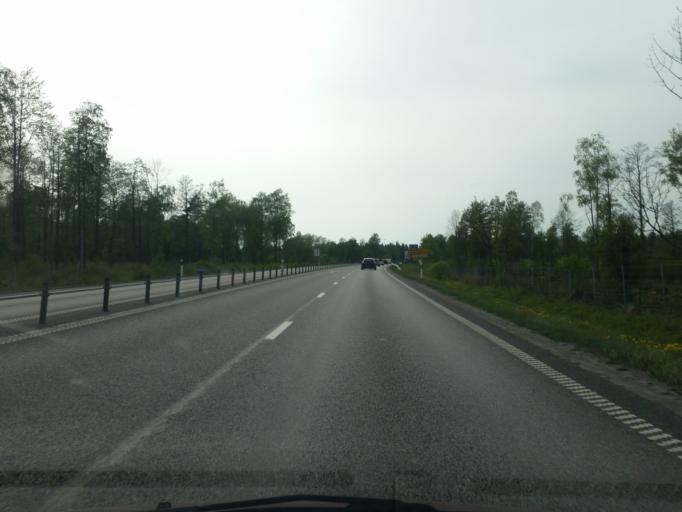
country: SE
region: Vaestra Goetaland
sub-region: Ulricehamns Kommun
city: Ulricehamn
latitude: 57.8006
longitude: 13.5125
